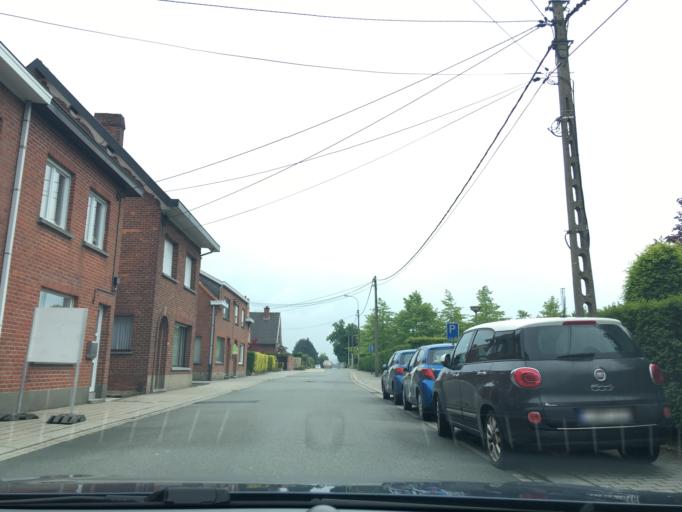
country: BE
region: Flanders
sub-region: Provincie West-Vlaanderen
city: Roeselare
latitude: 50.9306
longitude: 3.1592
